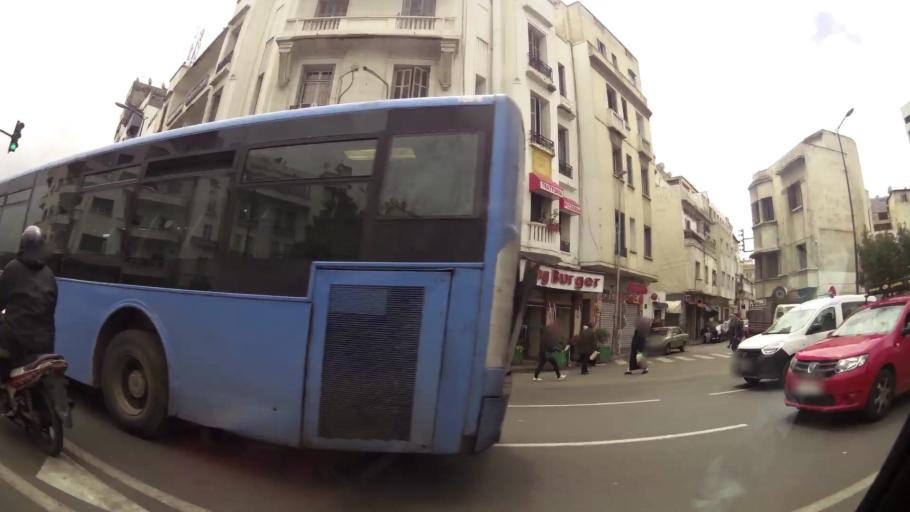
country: MA
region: Grand Casablanca
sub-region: Casablanca
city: Casablanca
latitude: 33.5952
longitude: -7.6256
